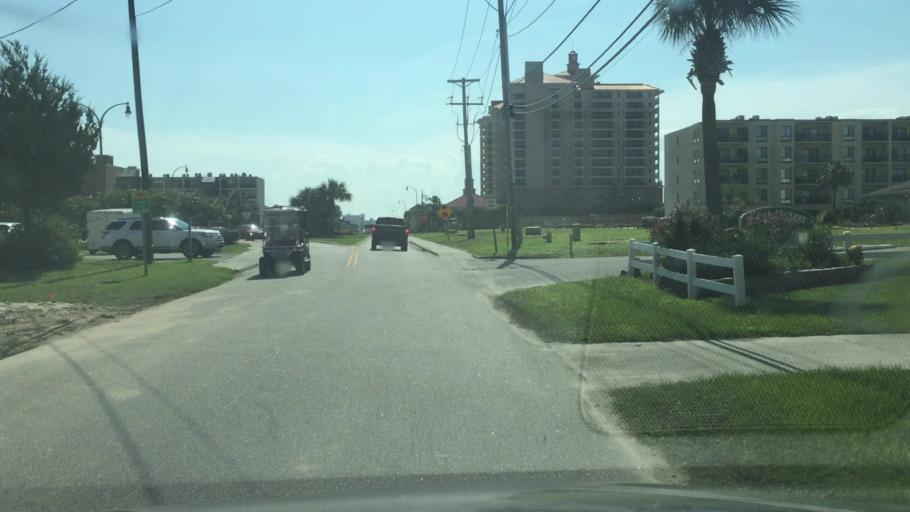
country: US
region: South Carolina
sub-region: Horry County
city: North Myrtle Beach
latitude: 33.8274
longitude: -78.6468
